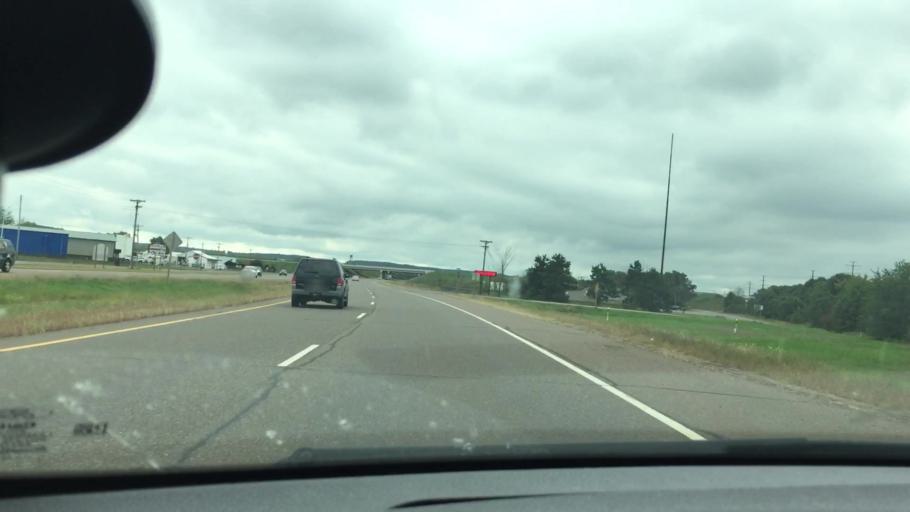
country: US
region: Wisconsin
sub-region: Chippewa County
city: Lake Hallie
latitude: 44.8994
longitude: -91.4150
